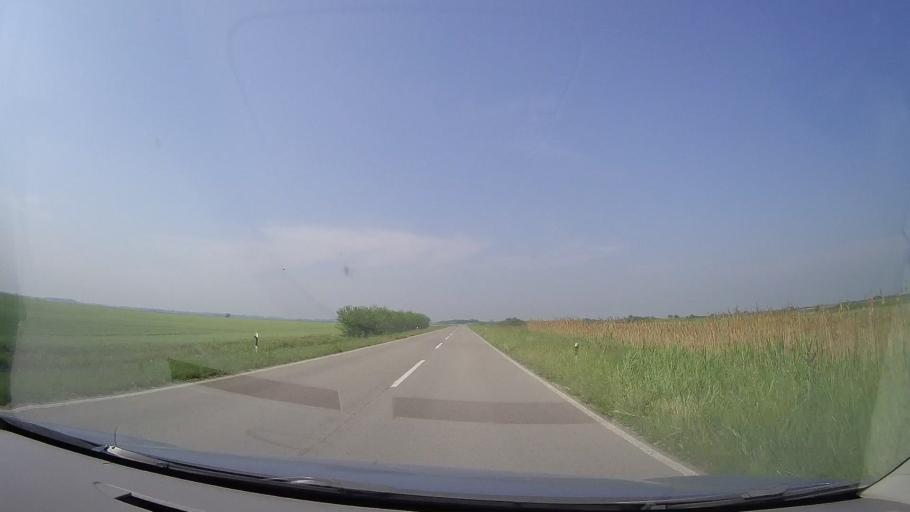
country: RS
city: Boka
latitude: 45.4025
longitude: 20.8165
